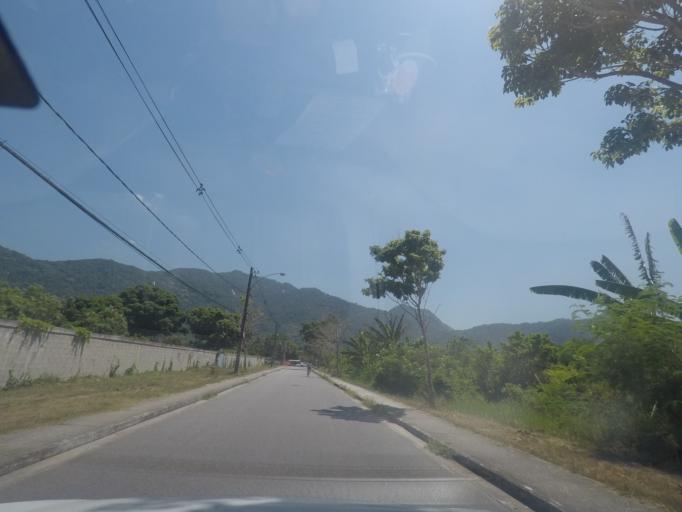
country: BR
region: Rio de Janeiro
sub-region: Nilopolis
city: Nilopolis
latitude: -22.9866
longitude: -43.4604
